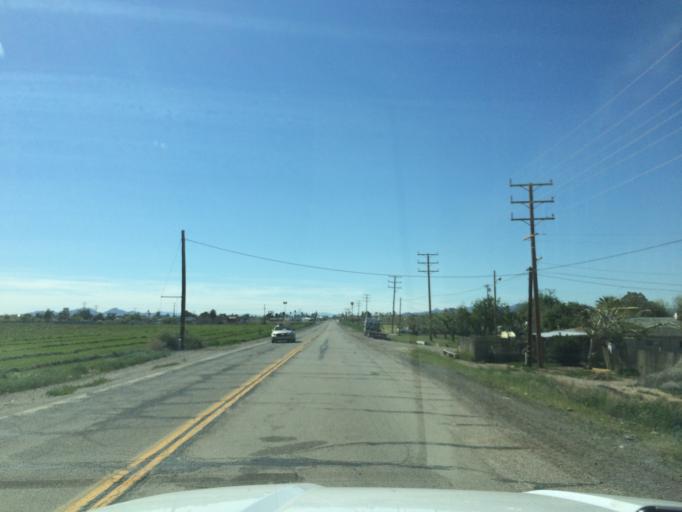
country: US
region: California
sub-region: Riverside County
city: Blythe
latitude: 33.6109
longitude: -114.5623
